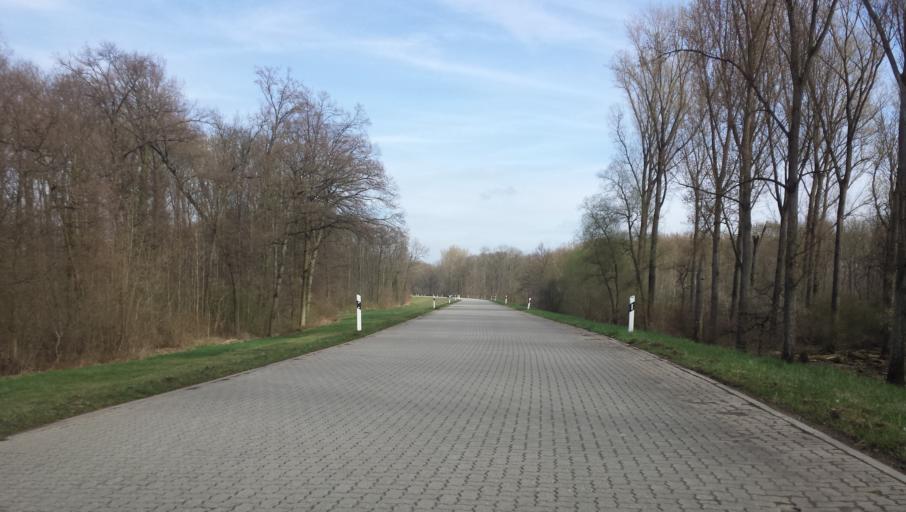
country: DE
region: Rheinland-Pfalz
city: Germersheim
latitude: 49.2588
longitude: 8.4091
